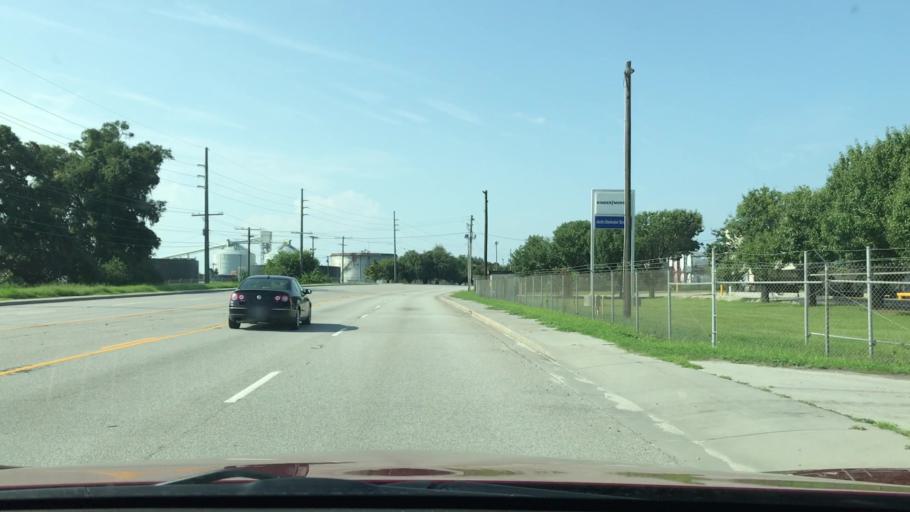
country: US
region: South Carolina
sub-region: Charleston County
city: North Charleston
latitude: 32.8885
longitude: -79.9729
